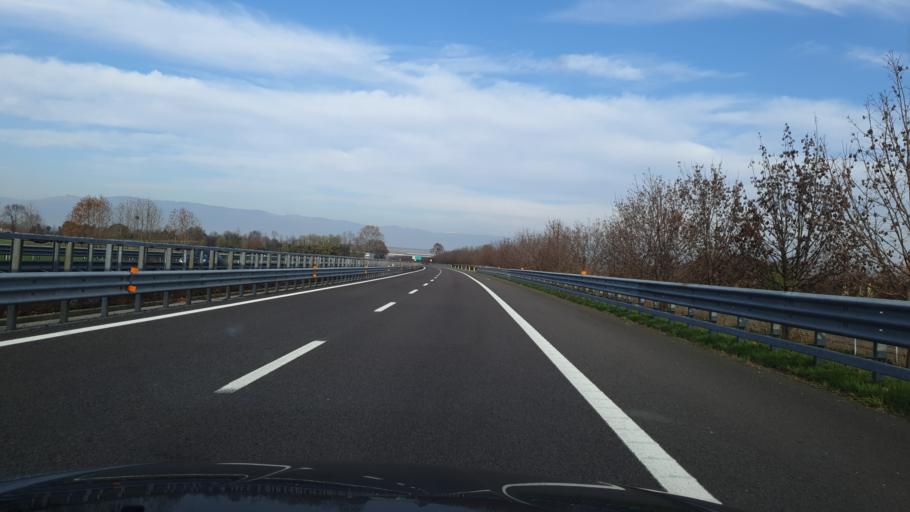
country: IT
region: Veneto
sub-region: Provincia di Vicenza
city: Vigardolo
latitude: 45.6069
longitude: 11.6006
